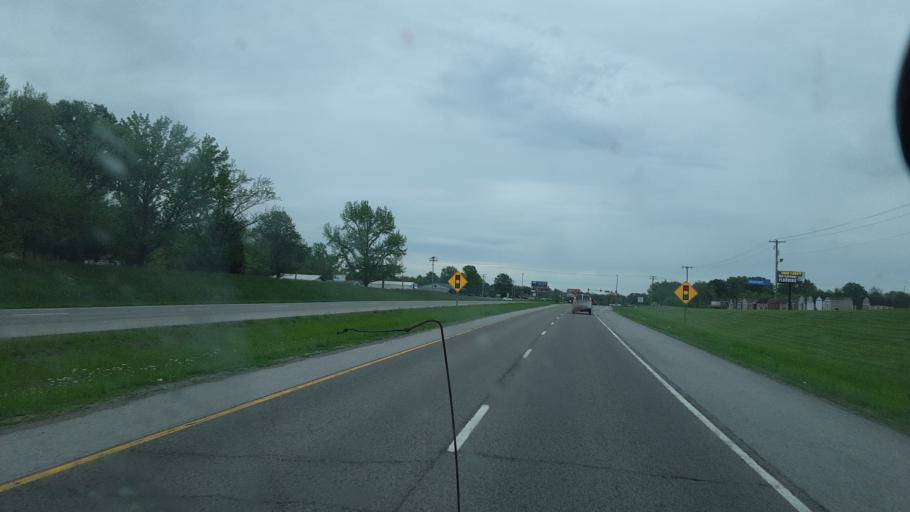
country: US
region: Illinois
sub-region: Jackson County
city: Murphysboro
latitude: 37.7626
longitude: -89.2838
